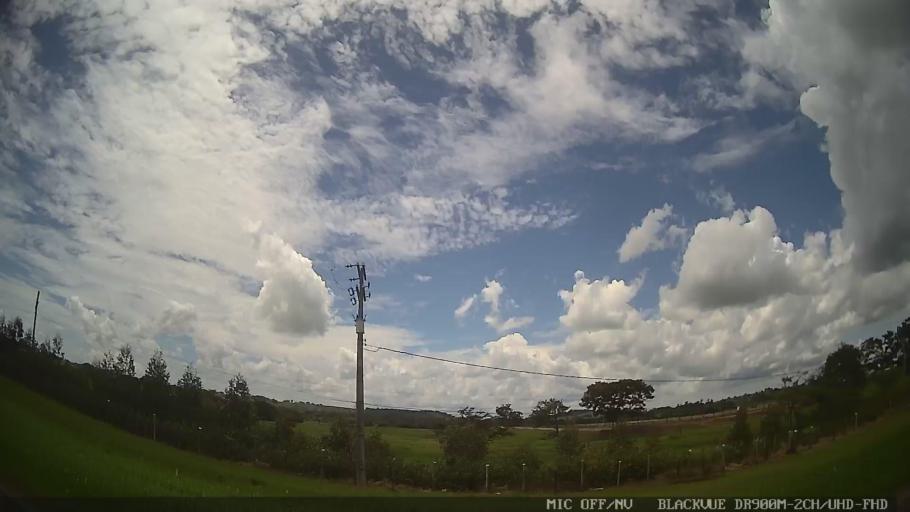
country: BR
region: Sao Paulo
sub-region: Conchas
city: Conchas
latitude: -23.0446
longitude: -47.9386
